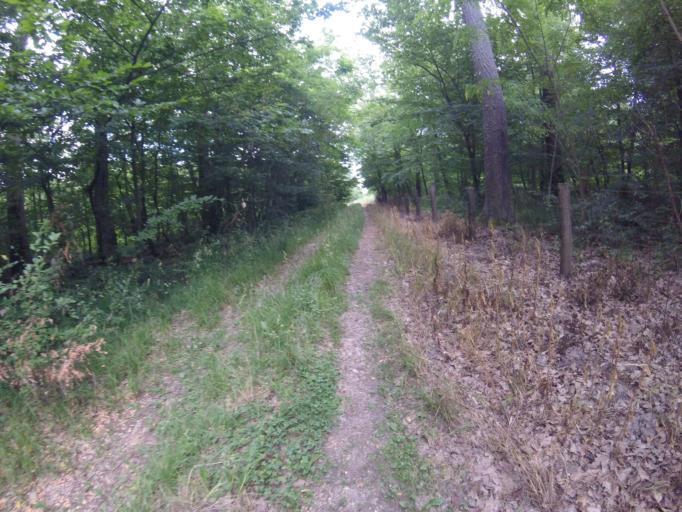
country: HU
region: Zala
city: Turje
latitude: 47.0424
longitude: 17.0256
